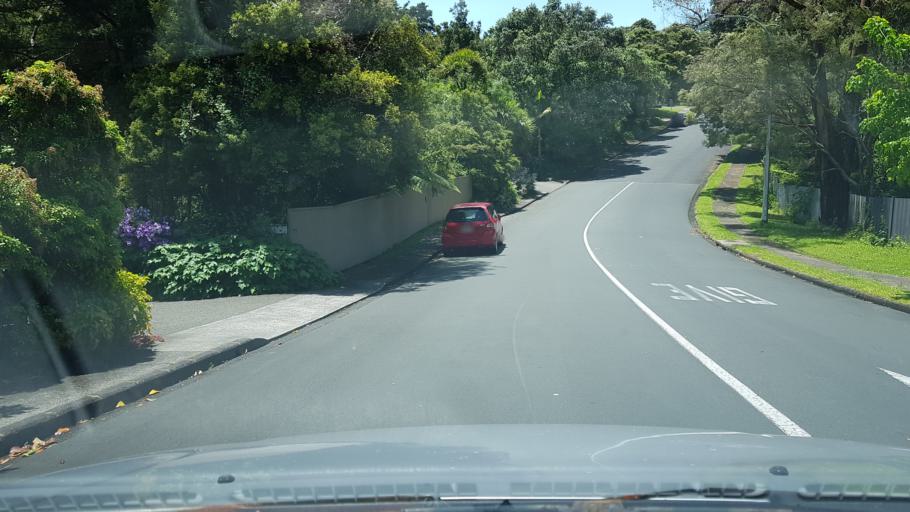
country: NZ
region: Auckland
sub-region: Auckland
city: North Shore
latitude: -36.8034
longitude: 174.7169
